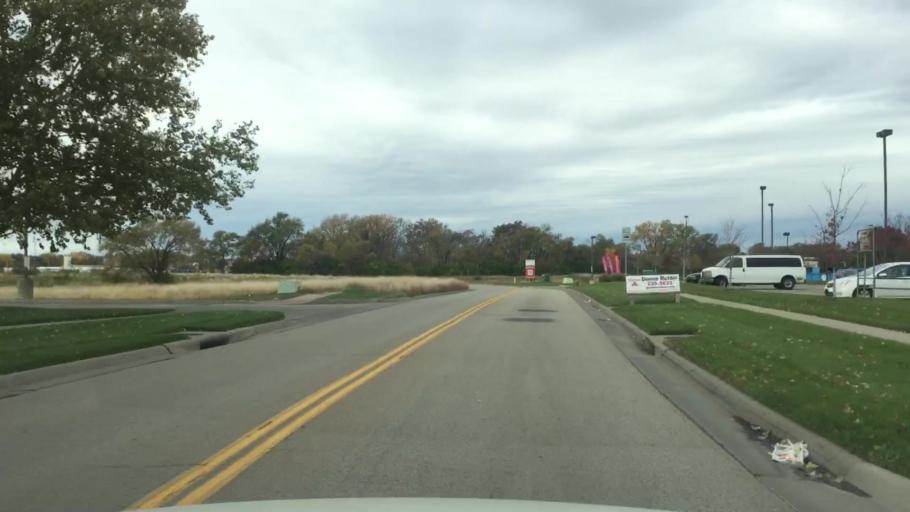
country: US
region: Kansas
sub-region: Shawnee County
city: Topeka
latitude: 39.0924
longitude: -95.6742
